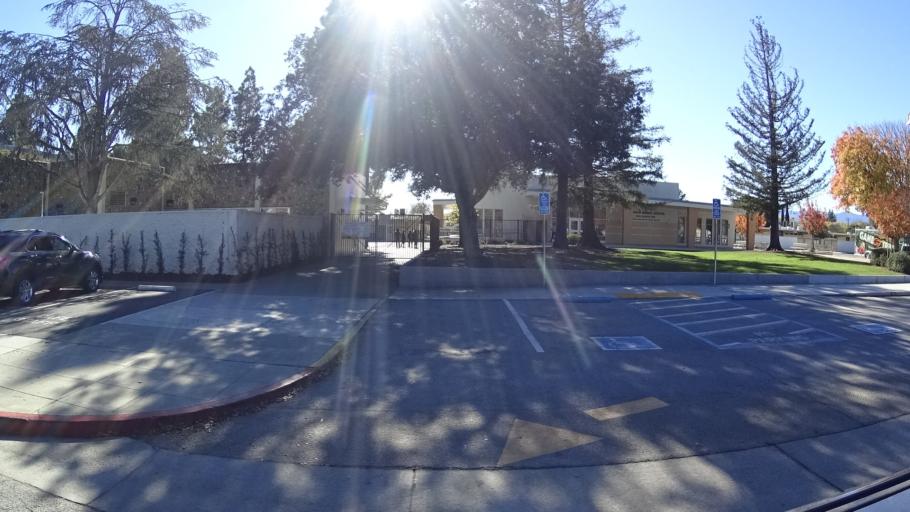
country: US
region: California
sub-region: Santa Clara County
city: Sunnyvale
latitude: 37.3499
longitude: -122.0086
